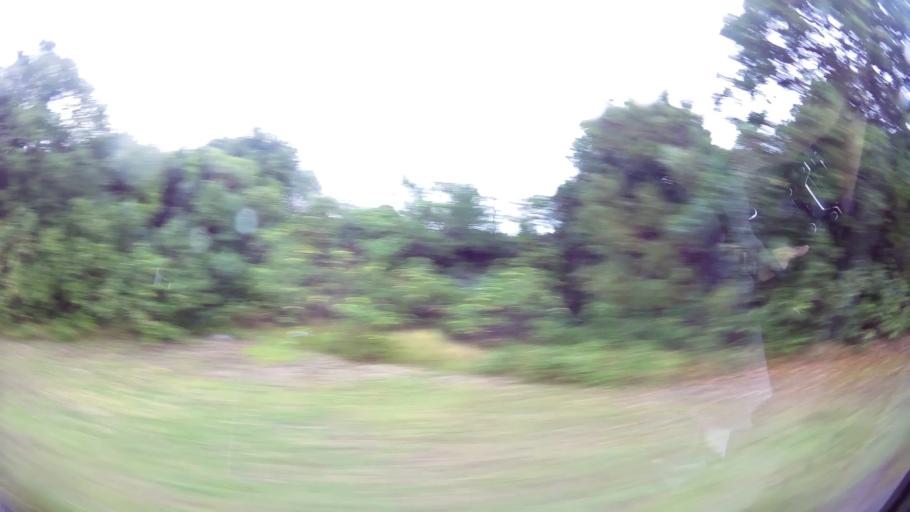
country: ZA
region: Eastern Cape
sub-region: Nelson Mandela Bay Metropolitan Municipality
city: Port Elizabeth
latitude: -34.0158
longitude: 25.5097
